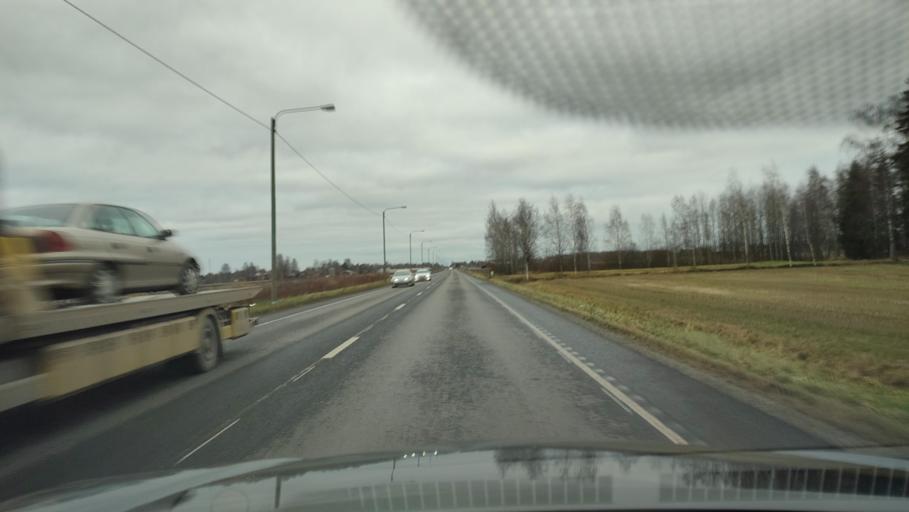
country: FI
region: Southern Ostrobothnia
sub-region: Seinaejoki
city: Ilmajoki
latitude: 62.7178
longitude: 22.5577
